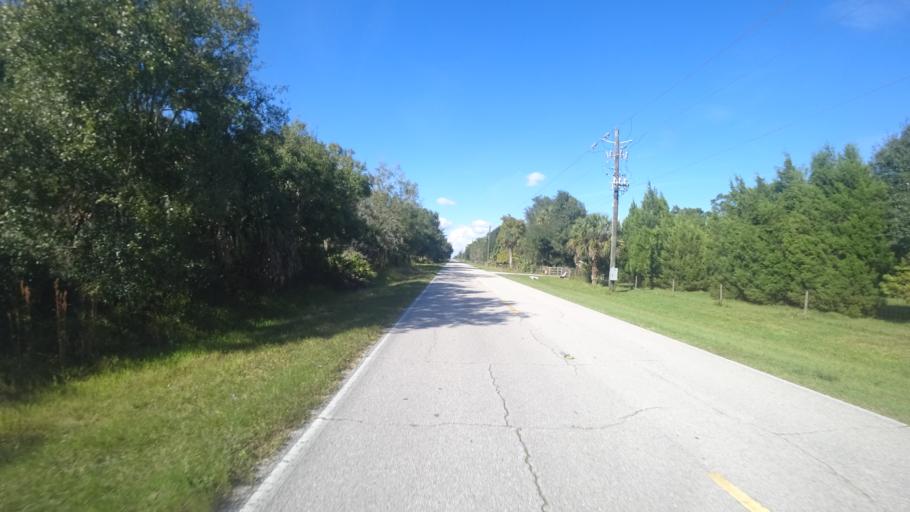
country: US
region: Florida
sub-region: Sarasota County
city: Fruitville
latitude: 27.4118
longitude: -82.2710
